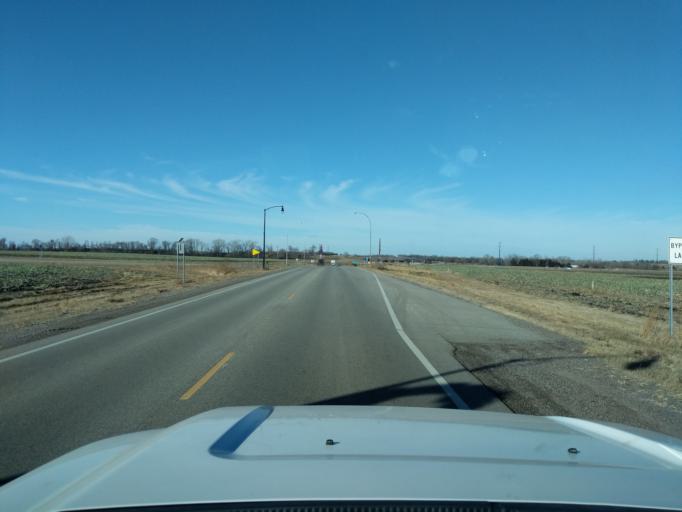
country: US
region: Minnesota
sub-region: Yellow Medicine County
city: Granite Falls
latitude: 44.7698
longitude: -95.5419
